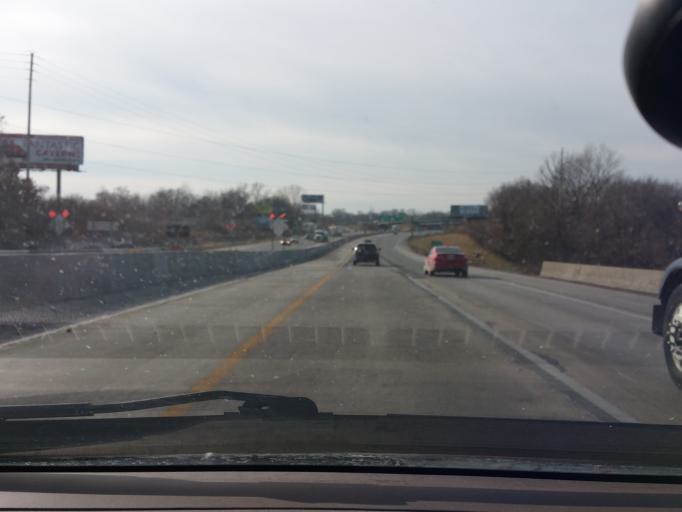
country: US
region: Missouri
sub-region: Clay County
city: Pleasant Valley
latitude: 39.2098
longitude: -94.4843
